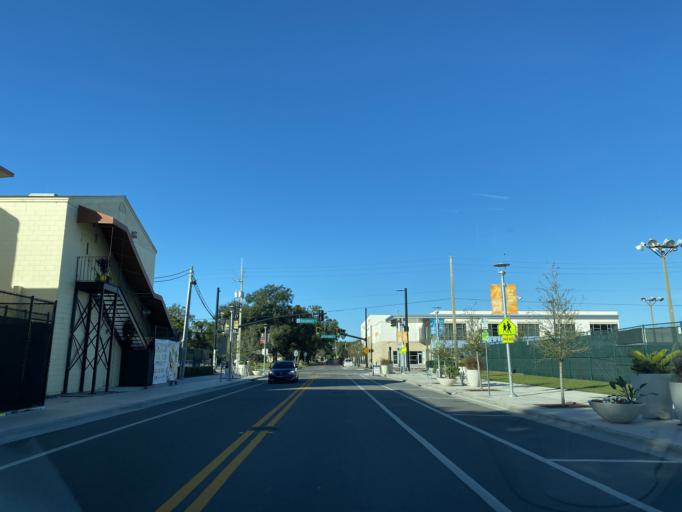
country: US
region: Florida
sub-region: Orange County
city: Orlando
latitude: 28.5476
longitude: -81.3883
